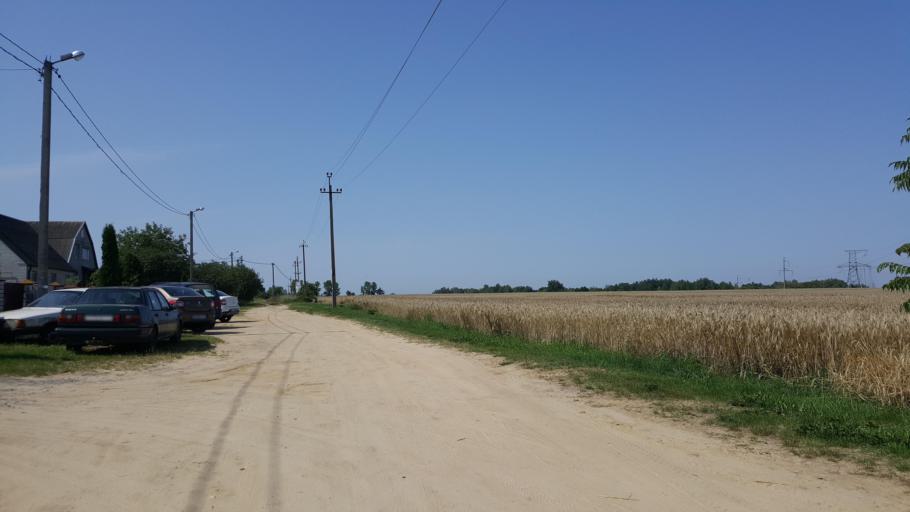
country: BY
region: Brest
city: Zhabinka
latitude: 52.2107
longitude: 23.9966
